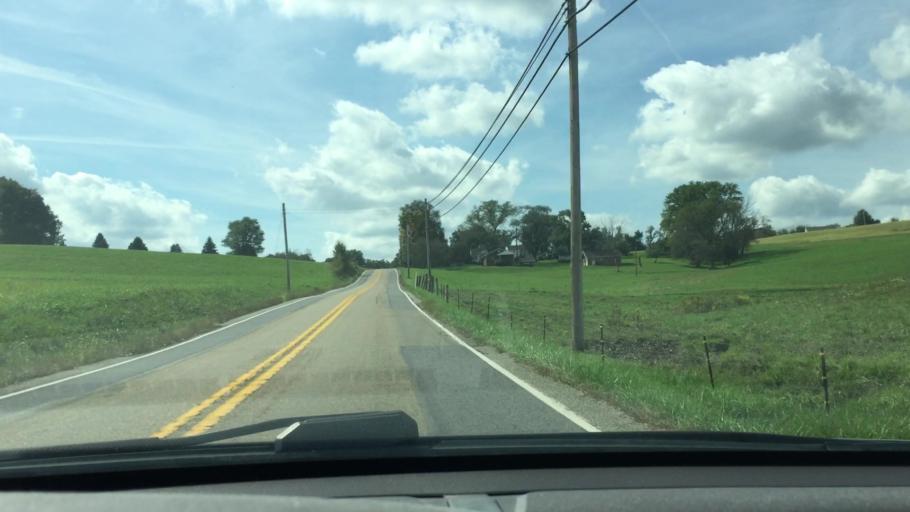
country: US
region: Pennsylvania
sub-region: Washington County
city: Thompsonville
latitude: 40.3027
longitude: -80.1414
